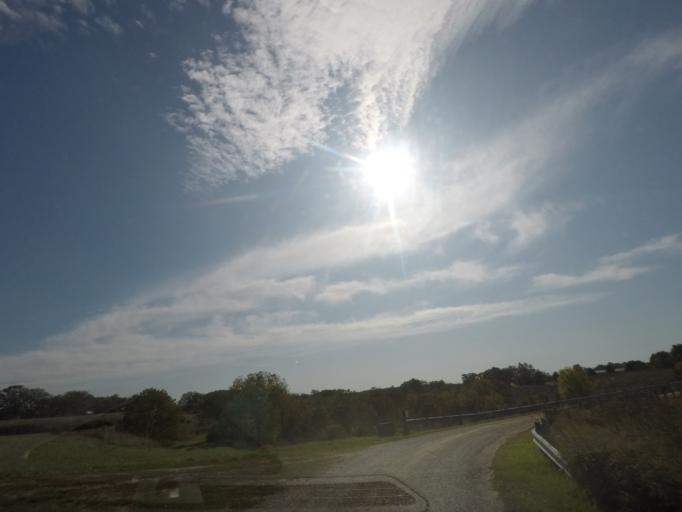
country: US
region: Iowa
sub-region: Story County
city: Gilbert
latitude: 42.1109
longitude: -93.5819
